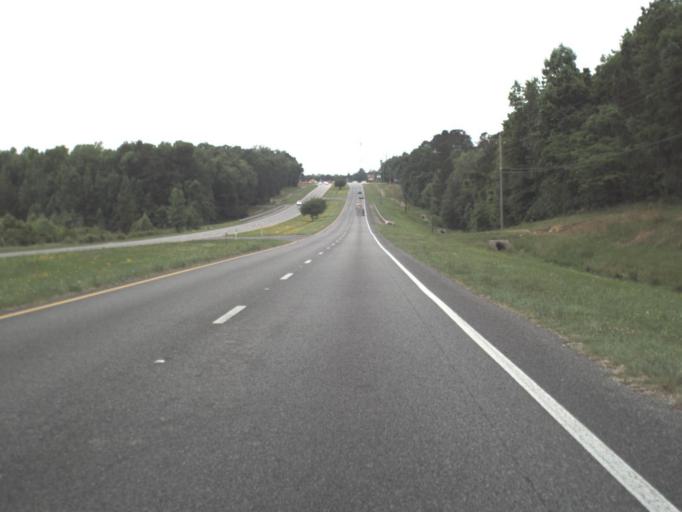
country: US
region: Florida
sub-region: Clay County
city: Middleburg
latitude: 30.0470
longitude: -81.8913
